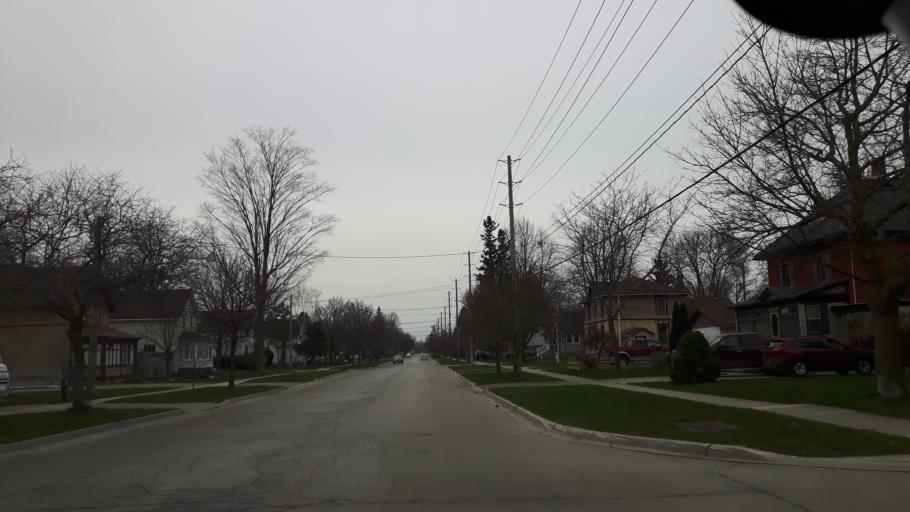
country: CA
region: Ontario
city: Goderich
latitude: 43.7473
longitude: -81.7046
